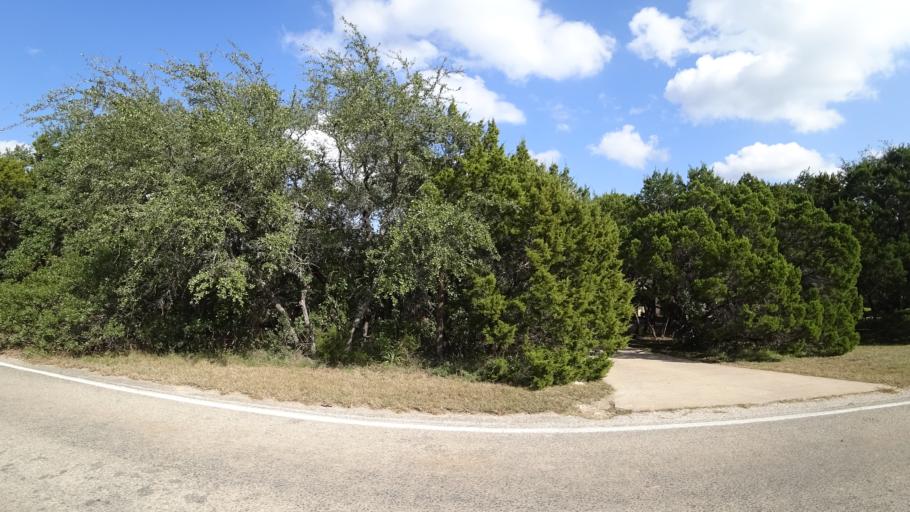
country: US
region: Texas
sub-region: Travis County
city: Barton Creek
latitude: 30.3074
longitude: -97.8656
